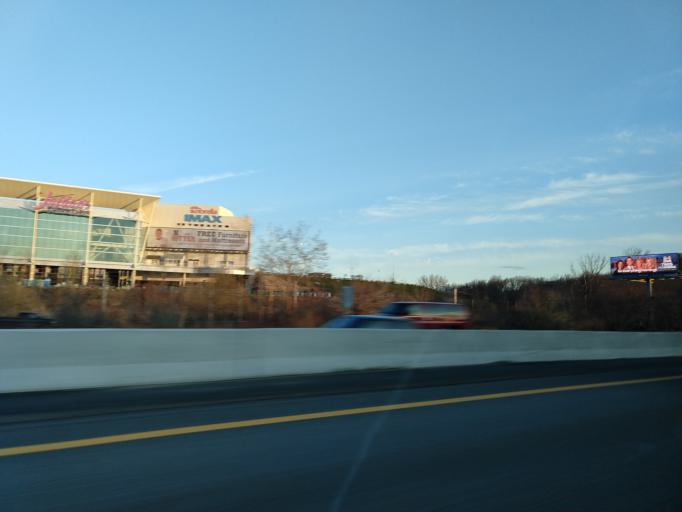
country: US
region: Massachusetts
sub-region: Middlesex County
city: Reading
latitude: 42.5190
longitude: -71.0881
